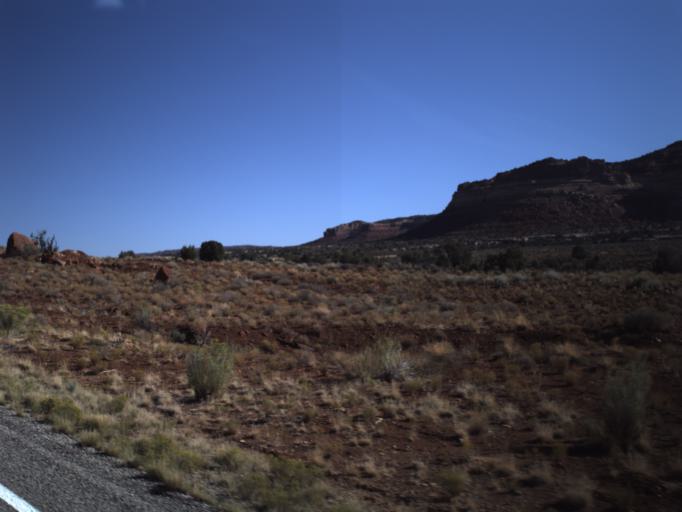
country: US
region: Utah
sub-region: San Juan County
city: Blanding
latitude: 37.7449
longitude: -110.2808
